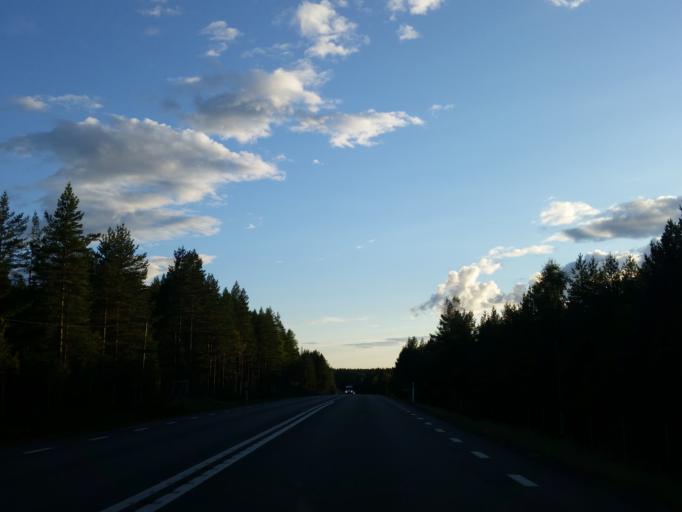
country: SE
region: Vaesterbotten
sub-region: Robertsfors Kommun
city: Robertsfors
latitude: 64.0158
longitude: 20.8272
